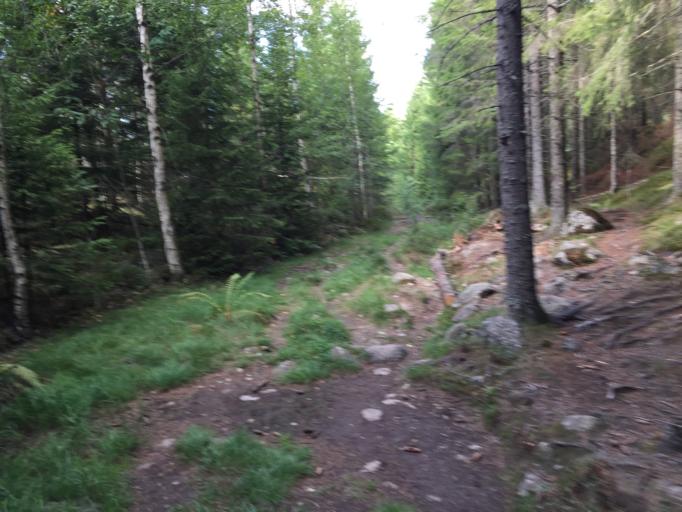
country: NO
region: Akershus
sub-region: Raelingen
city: Fjerdingby
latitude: 59.9156
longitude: 11.0285
